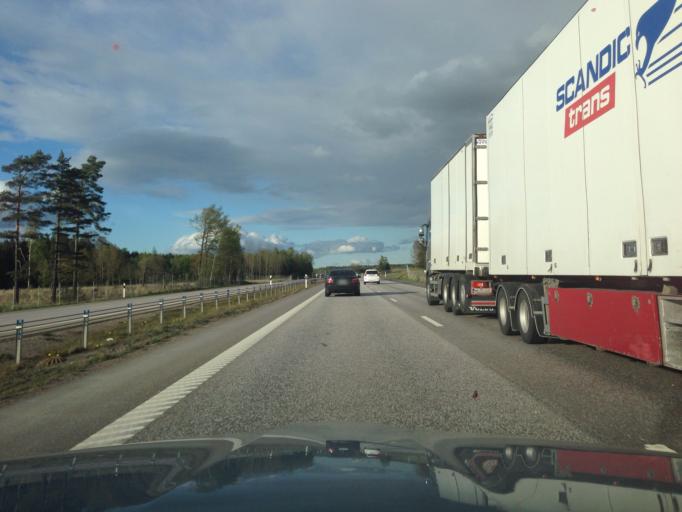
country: SE
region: OEstergoetland
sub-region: Linkopings Kommun
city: Vikingstad
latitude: 58.4067
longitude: 15.4517
